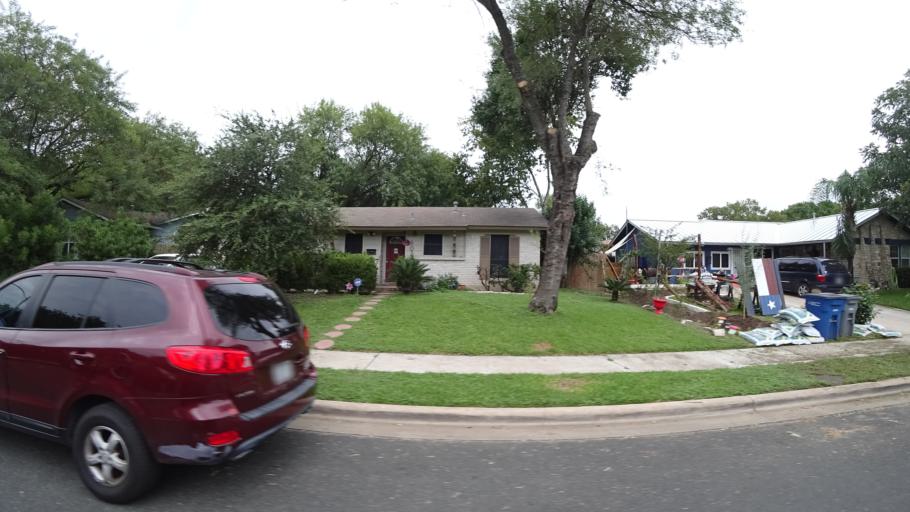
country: US
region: Texas
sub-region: Travis County
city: Rollingwood
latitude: 30.2146
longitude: -97.7807
